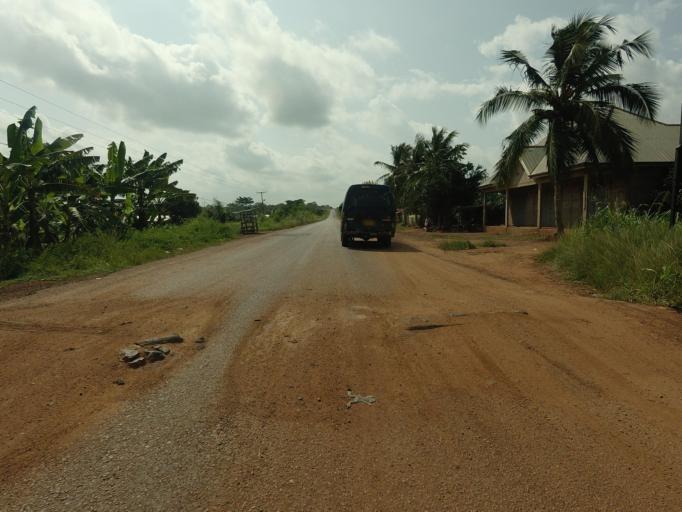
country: TG
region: Maritime
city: Tsevie
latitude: 6.3701
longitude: 0.8496
